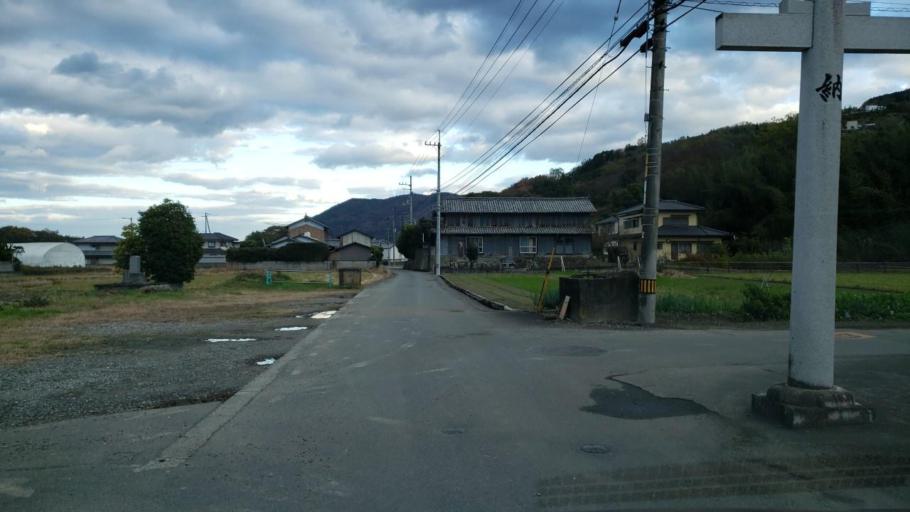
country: JP
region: Tokushima
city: Wakimachi
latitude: 34.0569
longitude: 134.1499
